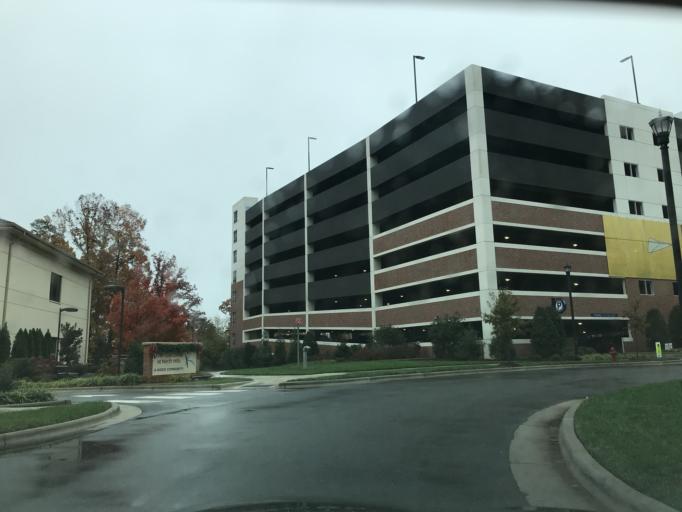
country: US
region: North Carolina
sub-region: Wake County
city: West Raleigh
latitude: 35.8353
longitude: -78.6355
